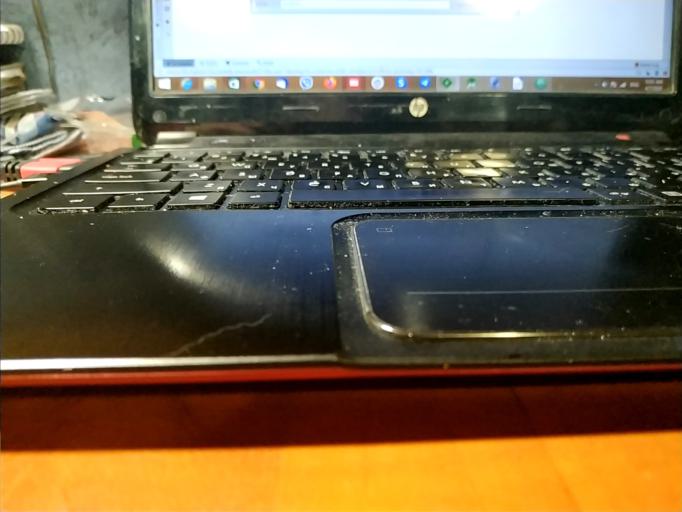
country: RU
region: Vologda
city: Suda
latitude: 58.9164
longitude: 37.5432
